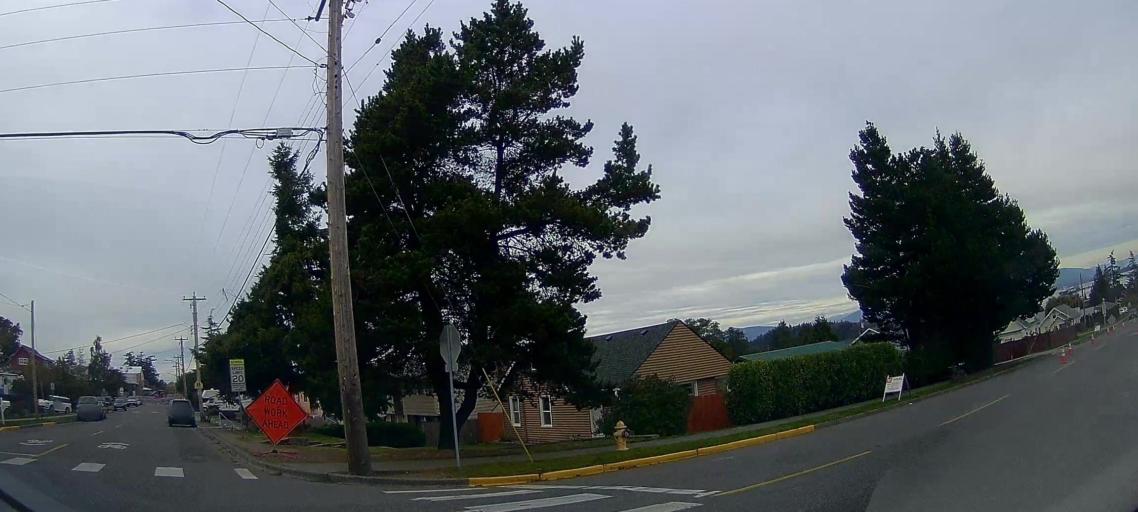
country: US
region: Washington
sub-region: Skagit County
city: Anacortes
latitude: 48.5048
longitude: -122.6219
